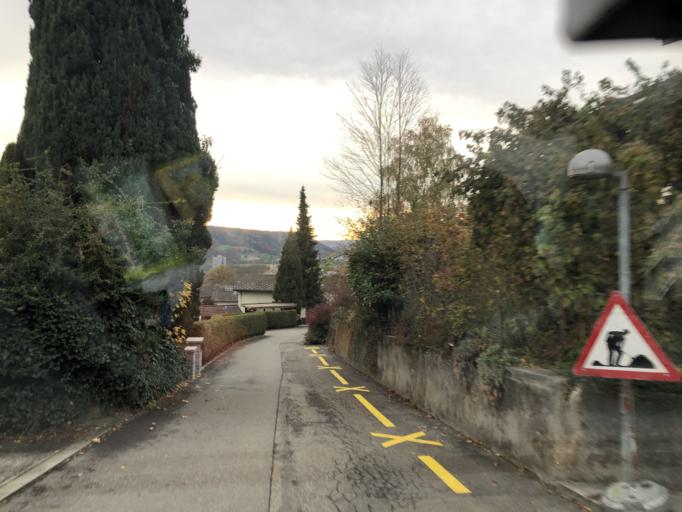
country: CH
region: Aargau
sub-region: Bezirk Baden
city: Obersiggenthal
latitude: 47.4872
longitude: 8.3029
